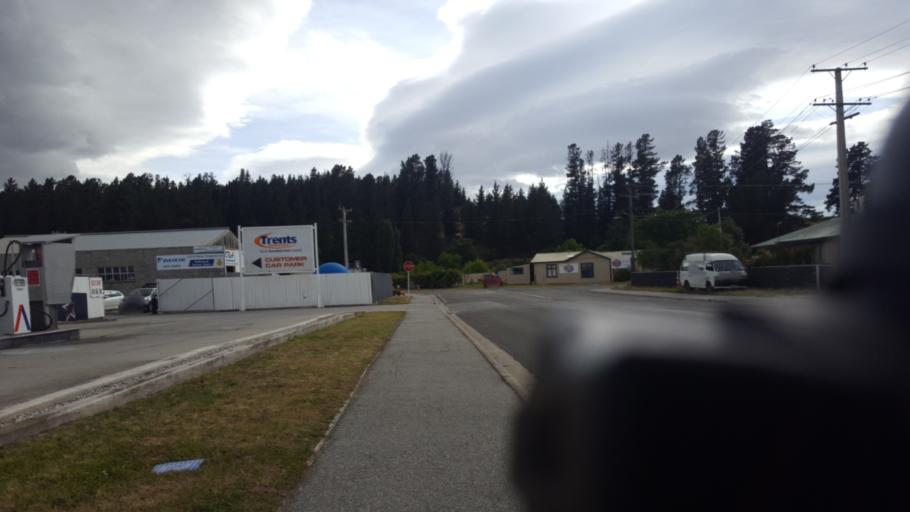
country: NZ
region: Otago
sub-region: Queenstown-Lakes District
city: Wanaka
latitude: -45.2448
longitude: 169.3947
